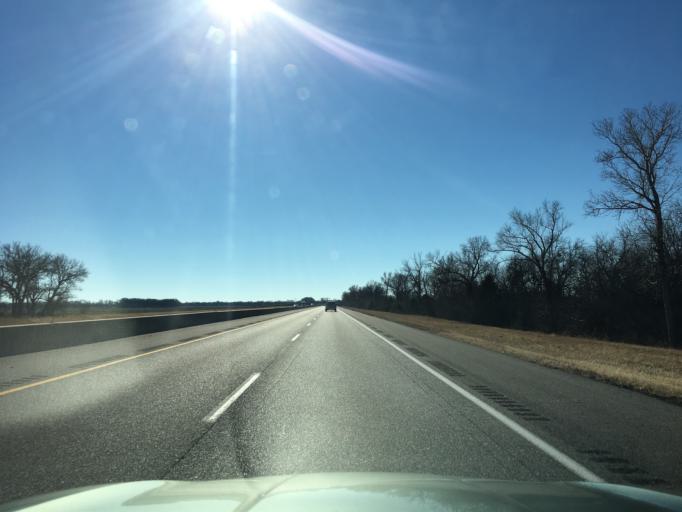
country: US
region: Kansas
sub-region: Sumner County
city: Belle Plaine
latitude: 37.4299
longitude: -97.3214
